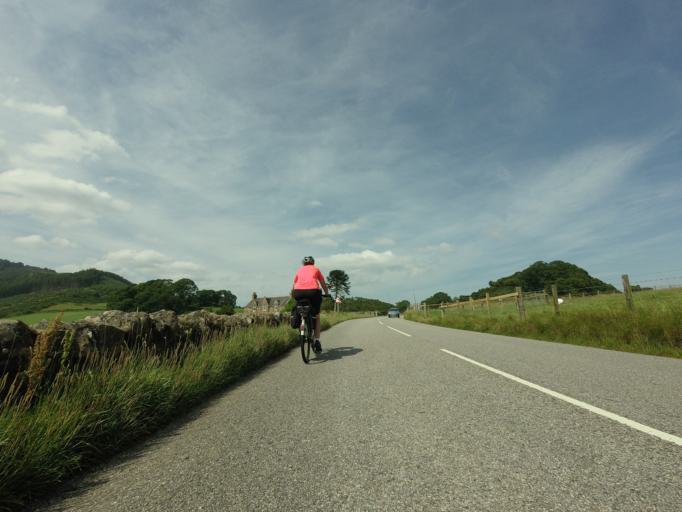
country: GB
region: Scotland
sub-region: Highland
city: Tain
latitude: 57.8489
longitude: -4.2028
